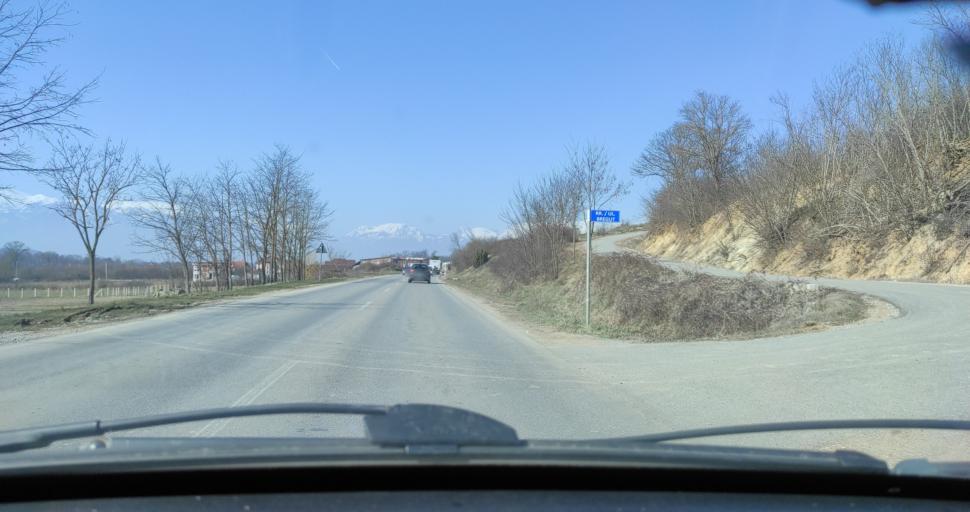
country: XK
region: Pec
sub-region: Komuna e Pejes
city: Kosuriq
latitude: 42.6169
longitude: 20.4936
